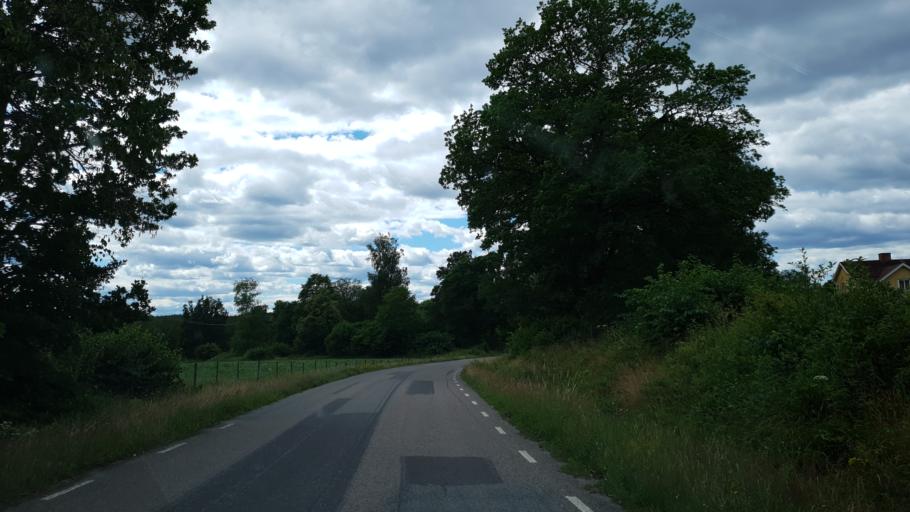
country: SE
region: Kalmar
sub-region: Hultsfreds Kommun
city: Virserum
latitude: 57.0471
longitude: 15.5861
